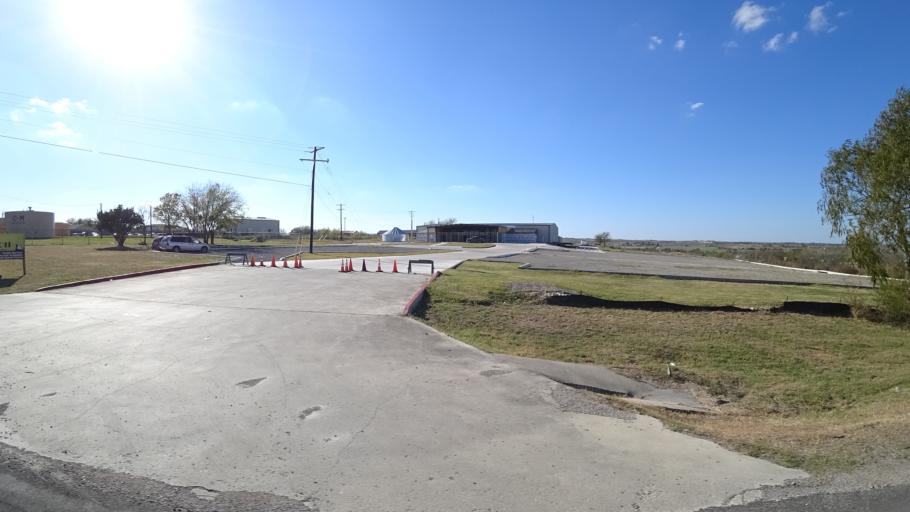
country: US
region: Texas
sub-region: Travis County
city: Onion Creek
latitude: 30.1175
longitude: -97.6953
